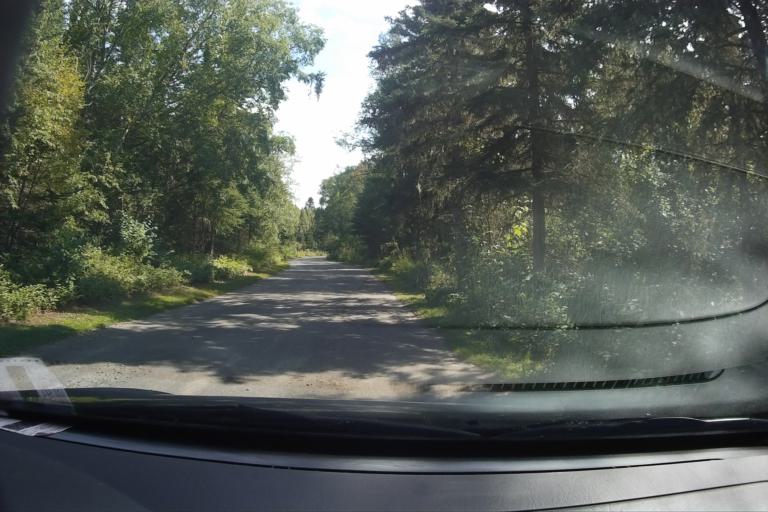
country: CA
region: Ontario
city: Marathon
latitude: 48.7900
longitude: -86.6269
